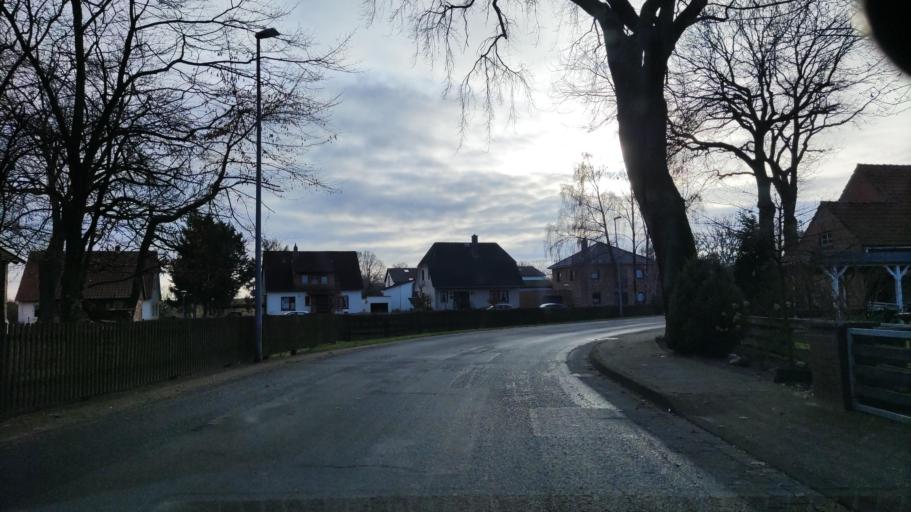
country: DE
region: Lower Saxony
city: Isernhagen Farster Bauerschaft
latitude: 52.5095
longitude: 9.9221
